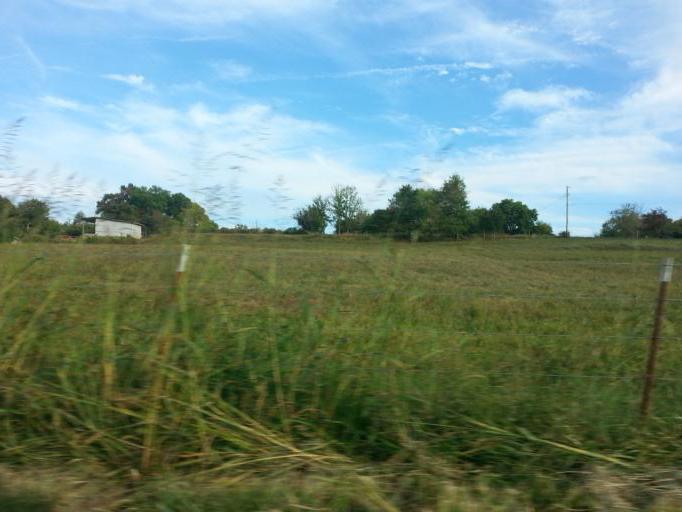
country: US
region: Tennessee
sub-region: Blount County
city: Wildwood
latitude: 35.8277
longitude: -83.8809
